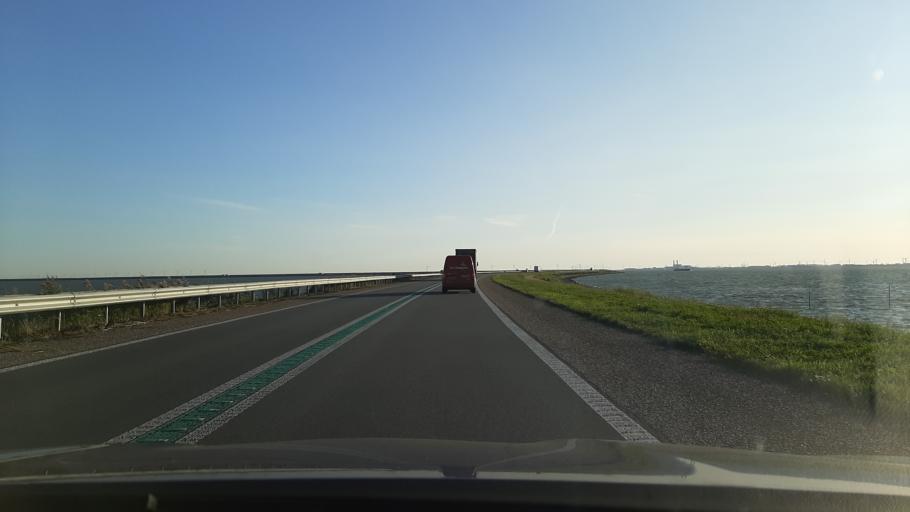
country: NL
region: Flevoland
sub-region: Gemeente Lelystad
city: Lelystad
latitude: 52.5618
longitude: 5.4491
